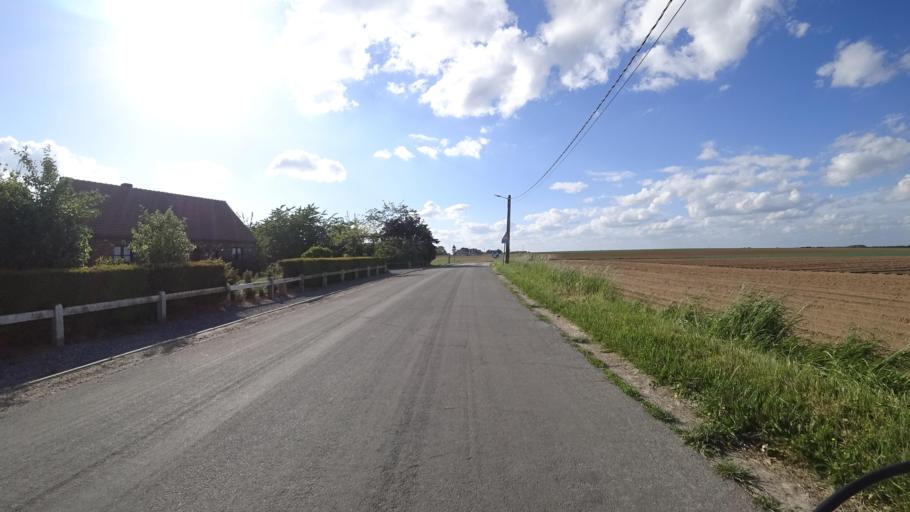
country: BE
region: Wallonia
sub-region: Province de Namur
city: Gembloux
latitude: 50.5369
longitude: 4.7475
